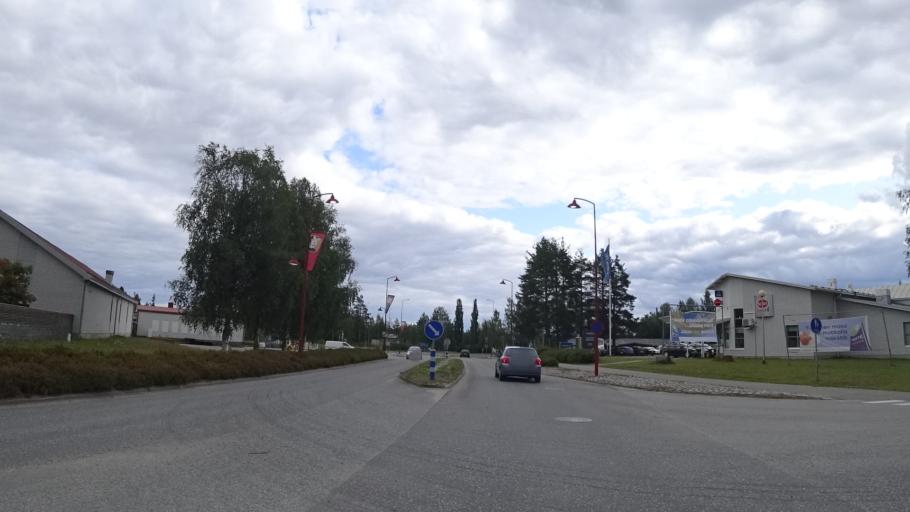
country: FI
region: North Karelia
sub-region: Joensuu
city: Ilomantsi
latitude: 62.6688
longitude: 30.9376
